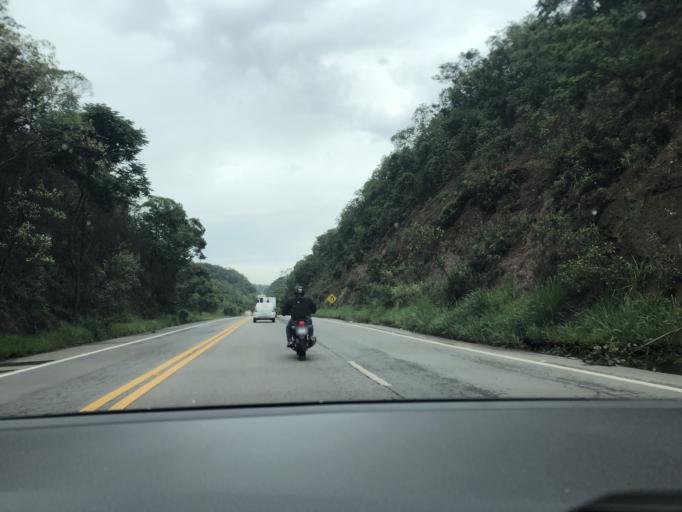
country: BR
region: Sao Paulo
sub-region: Jarinu
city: Jarinu
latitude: -23.1540
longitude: -46.7460
